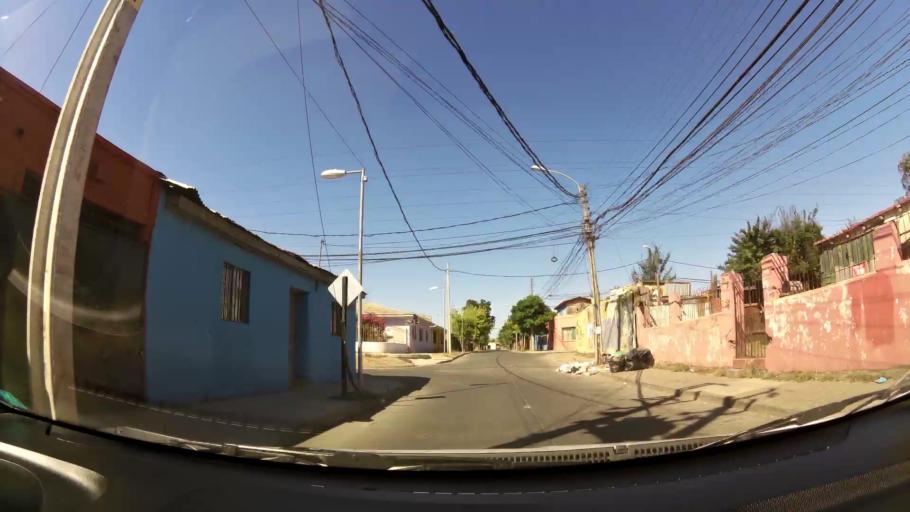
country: CL
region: O'Higgins
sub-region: Provincia de Cachapoal
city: Rancagua
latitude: -34.1785
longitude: -70.7495
